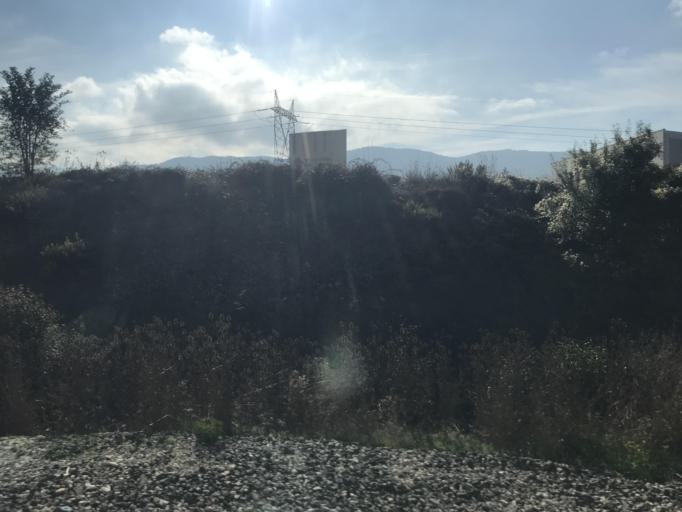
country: ES
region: Basque Country
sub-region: Provincia de Alava
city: Gasteiz / Vitoria
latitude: 42.8187
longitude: -2.7918
